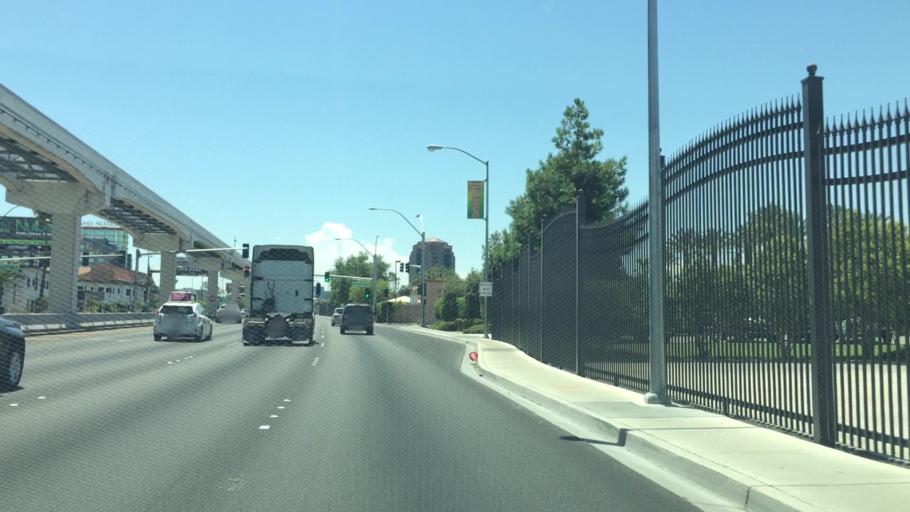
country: US
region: Nevada
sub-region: Clark County
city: Paradise
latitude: 36.1277
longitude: -115.1551
